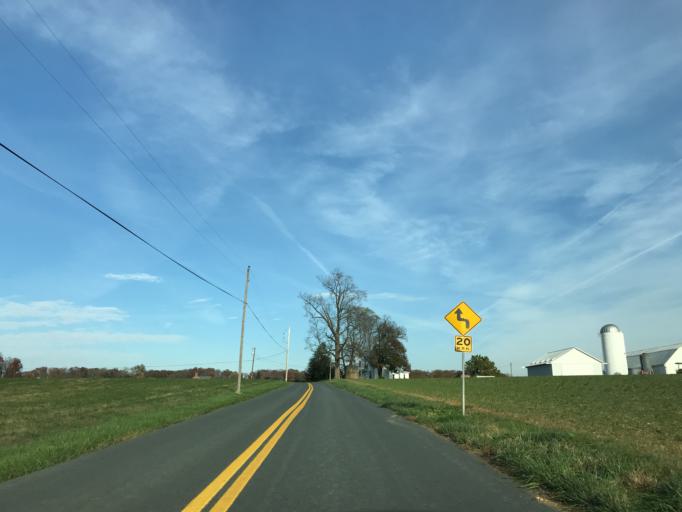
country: US
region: Maryland
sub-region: Carroll County
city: Hampstead
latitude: 39.5687
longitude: -76.7869
